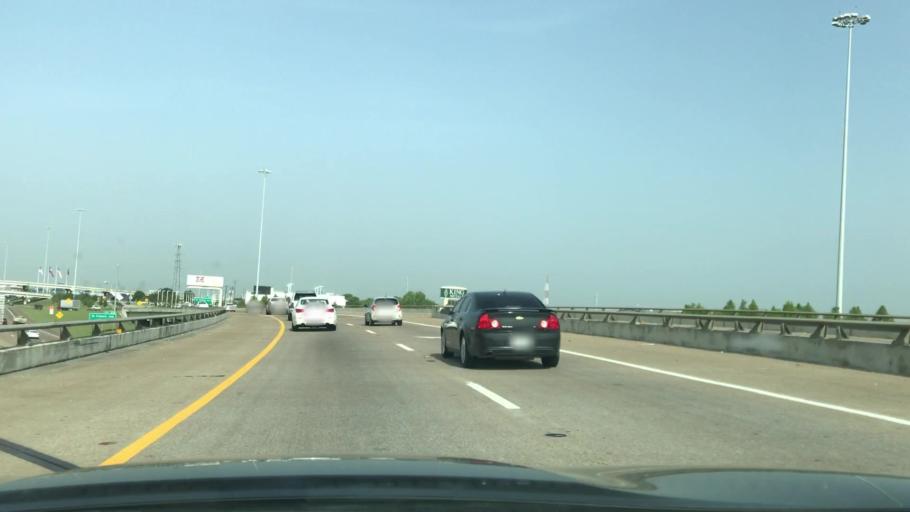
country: US
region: Texas
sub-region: Dallas County
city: Mesquite
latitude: 32.7994
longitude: -96.6758
